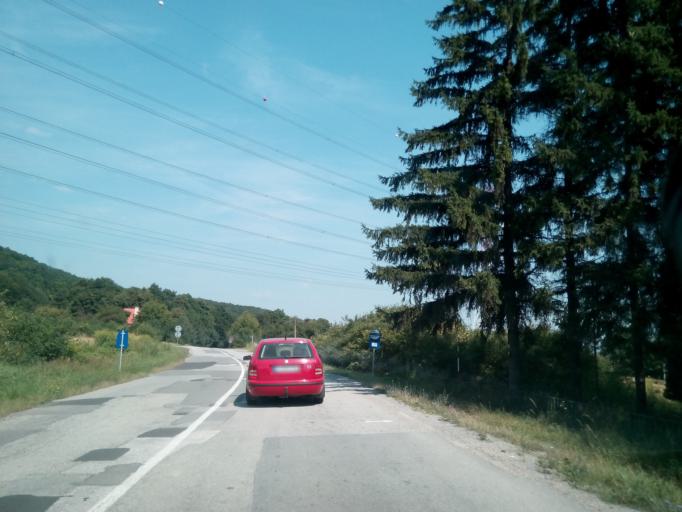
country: SK
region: Kosicky
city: Kosice
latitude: 48.7748
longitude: 21.2389
